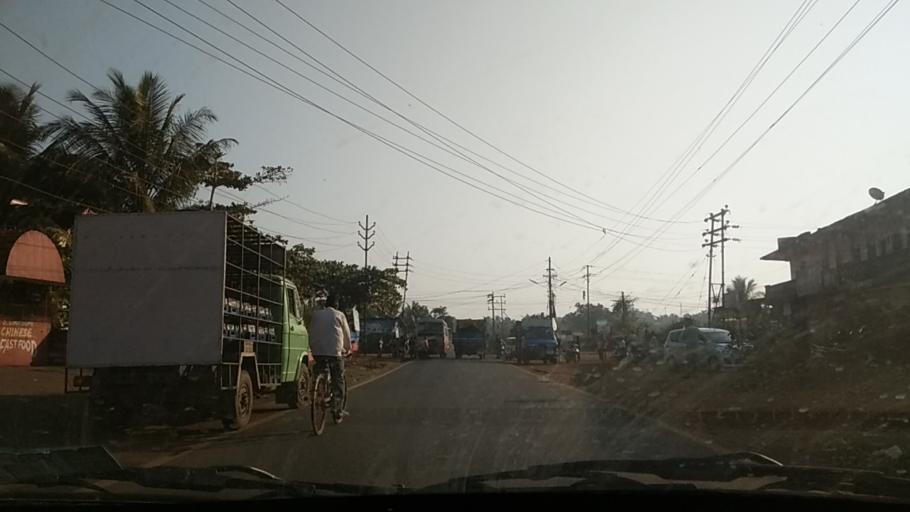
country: IN
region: Goa
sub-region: South Goa
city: Cuncolim
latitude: 15.1860
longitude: 74.0214
